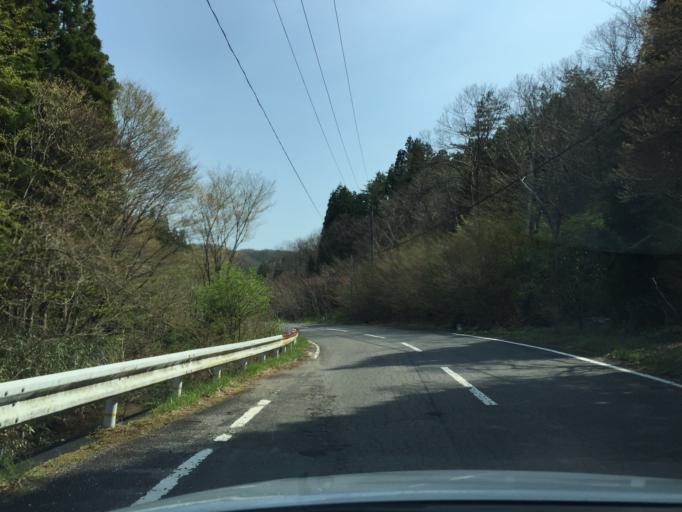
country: JP
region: Fukushima
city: Iwaki
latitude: 37.2344
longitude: 140.8453
